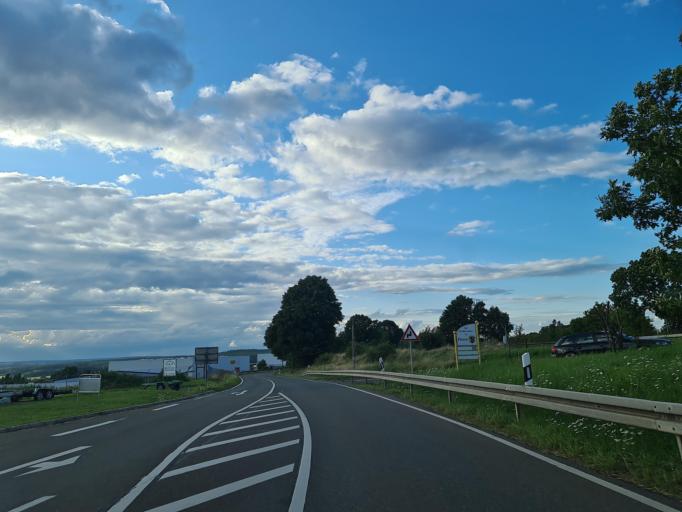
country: DE
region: Saxony
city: Pausa
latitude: 50.5882
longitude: 11.9987
